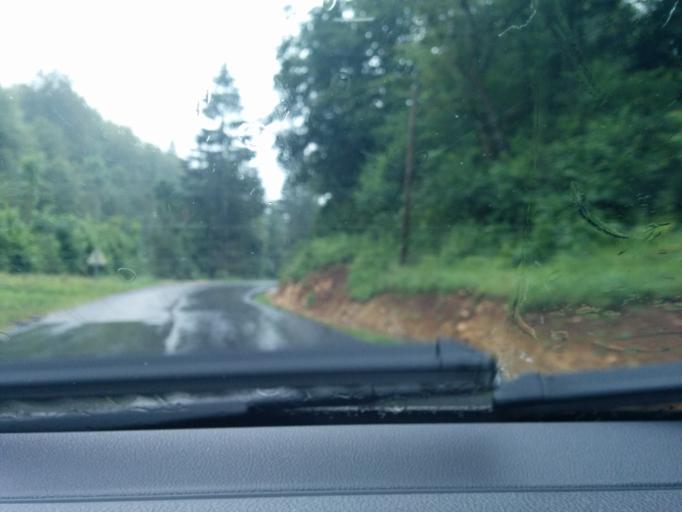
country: FR
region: Franche-Comte
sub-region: Departement du Jura
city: Valfin-les-Saint-Claude
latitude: 46.4610
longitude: 5.8324
